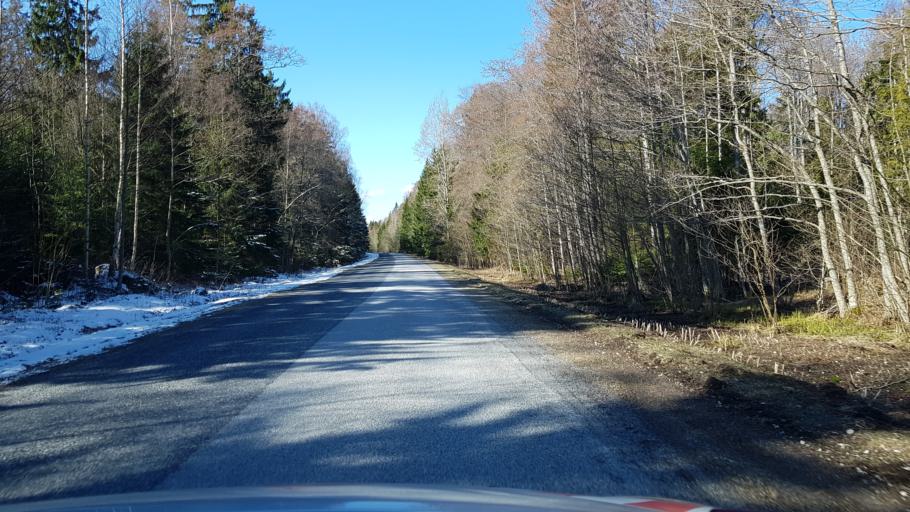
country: EE
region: Harju
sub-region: Loksa linn
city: Loksa
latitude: 59.5626
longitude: 25.8541
